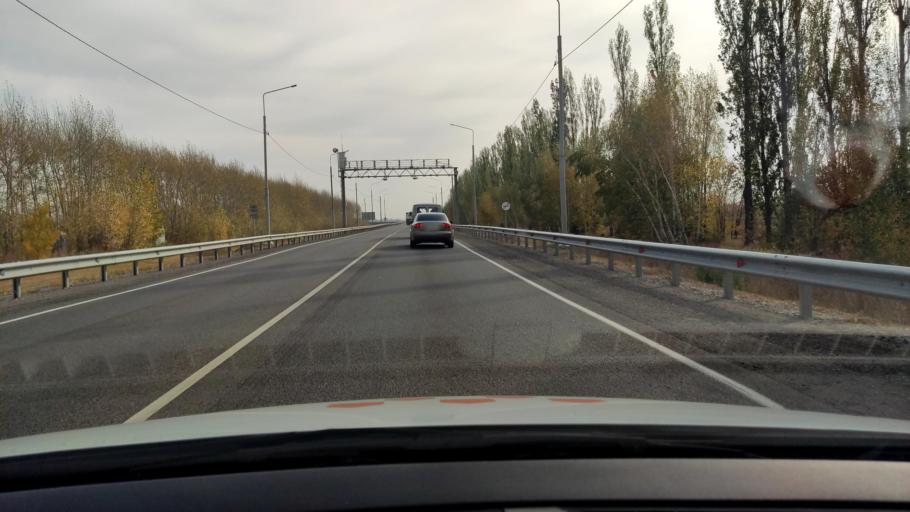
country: RU
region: Voronezj
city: Volya
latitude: 51.6892
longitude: 39.5044
